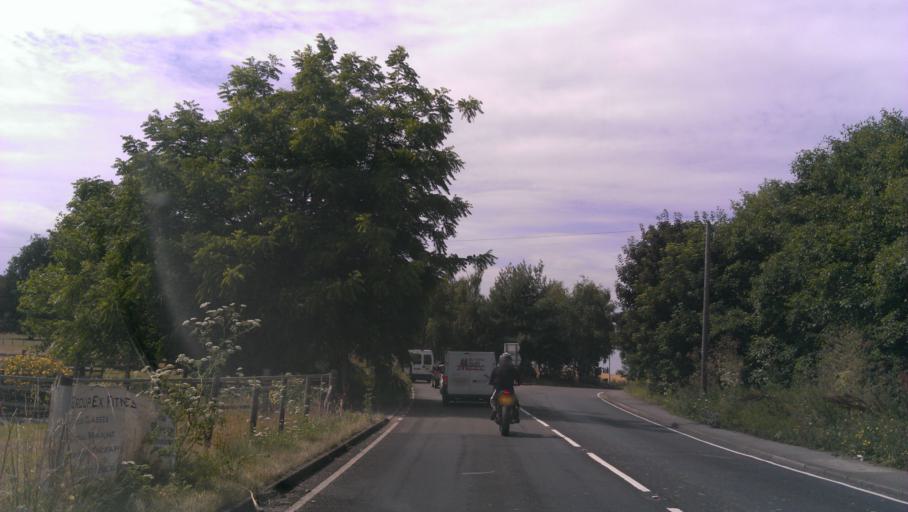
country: GB
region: England
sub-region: Kent
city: Faversham
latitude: 51.3134
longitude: 0.8658
